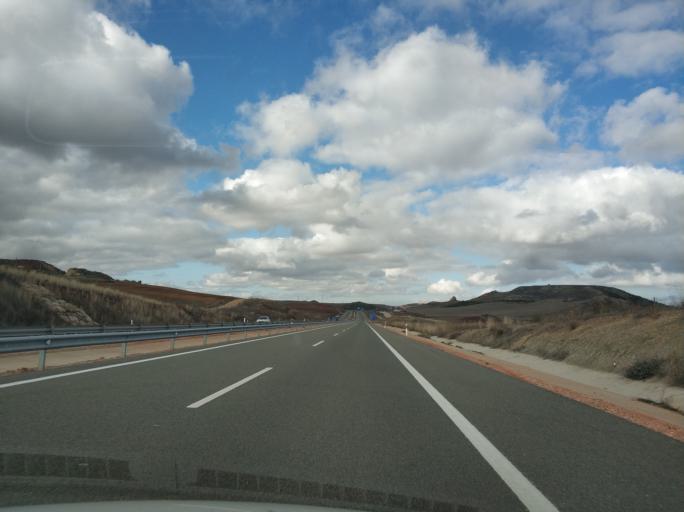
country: ES
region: Castille and Leon
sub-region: Provincia de Soria
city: Medinaceli
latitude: 41.2026
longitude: -2.4614
